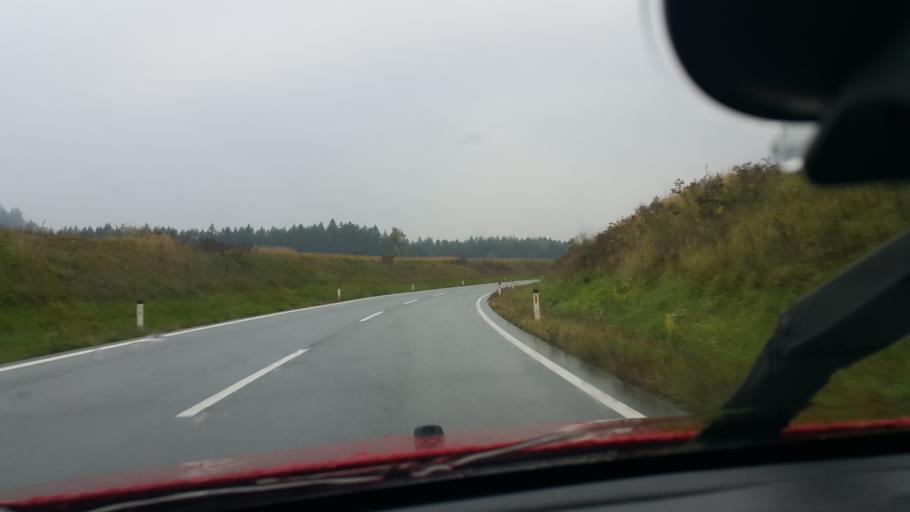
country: AT
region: Carinthia
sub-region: Politischer Bezirk Volkermarkt
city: Ruden
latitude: 46.6516
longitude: 14.7664
